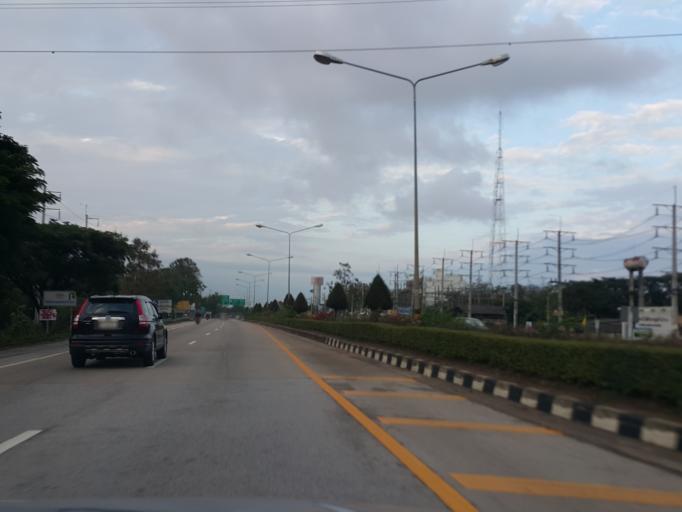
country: TH
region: Lampang
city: Lampang
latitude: 18.2487
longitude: 99.4511
